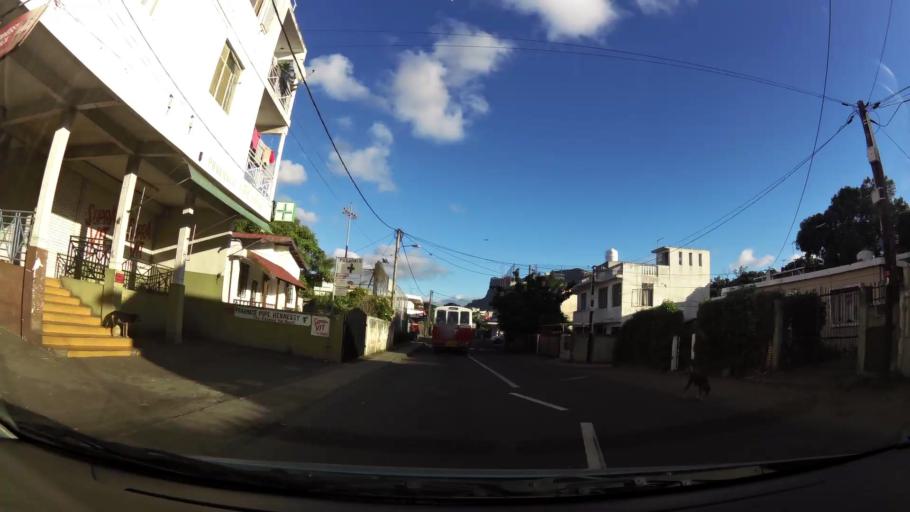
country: MU
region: Plaines Wilhems
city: Ebene
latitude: -20.2332
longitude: 57.4630
